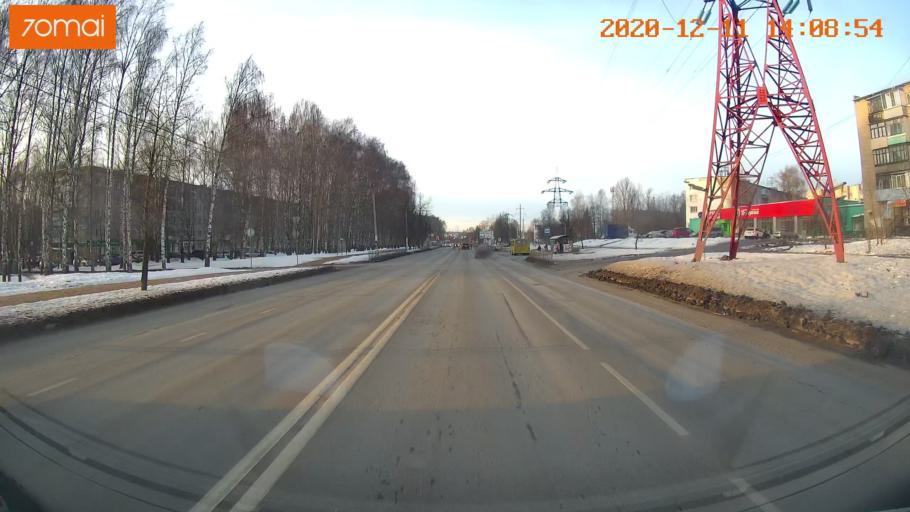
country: RU
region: Kostroma
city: Oktyabr'skiy
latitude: 57.7378
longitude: 40.9913
